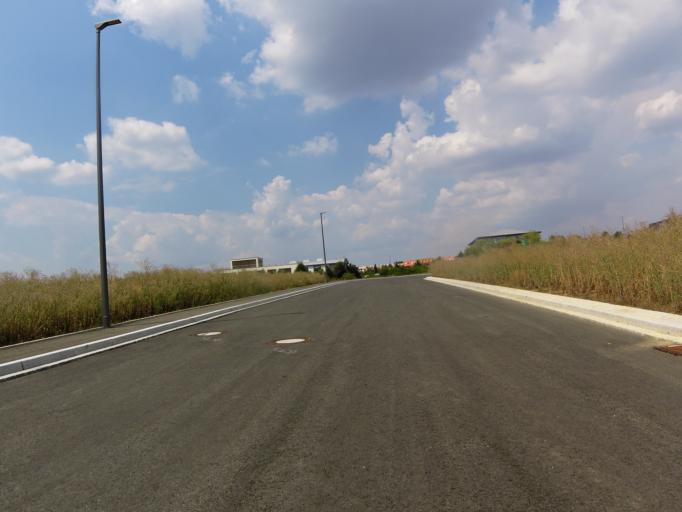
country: DE
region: Bavaria
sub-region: Regierungsbezirk Unterfranken
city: Eibelstadt
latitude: 49.7275
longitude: 9.9599
